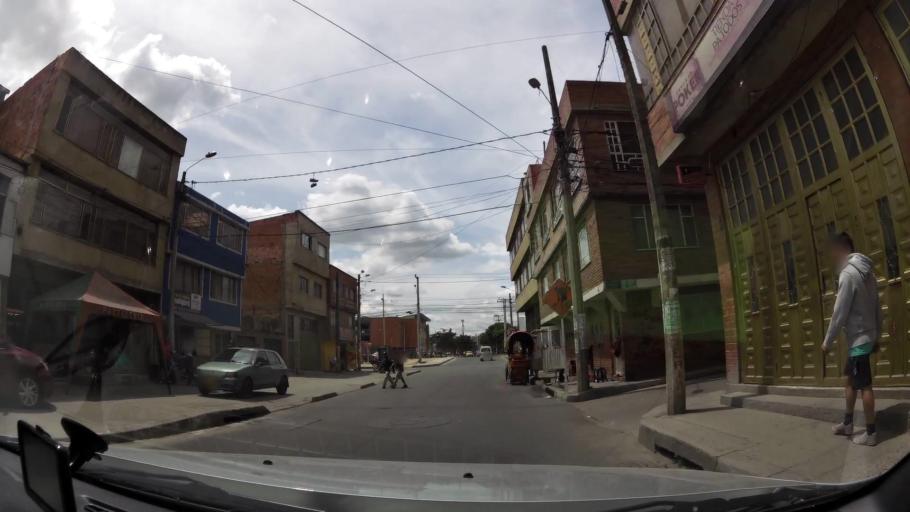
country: CO
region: Cundinamarca
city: Soacha
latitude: 4.6416
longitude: -74.1630
